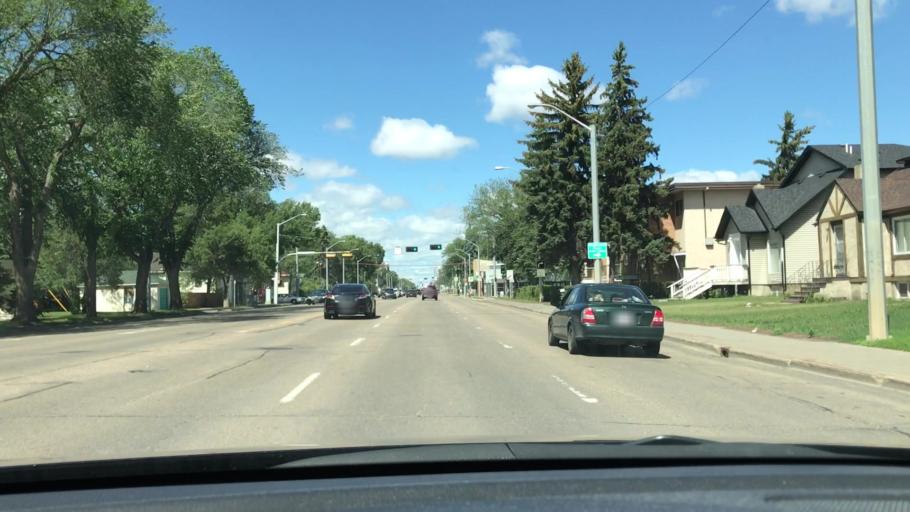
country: CA
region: Alberta
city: Edmonton
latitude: 53.5130
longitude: -113.5119
